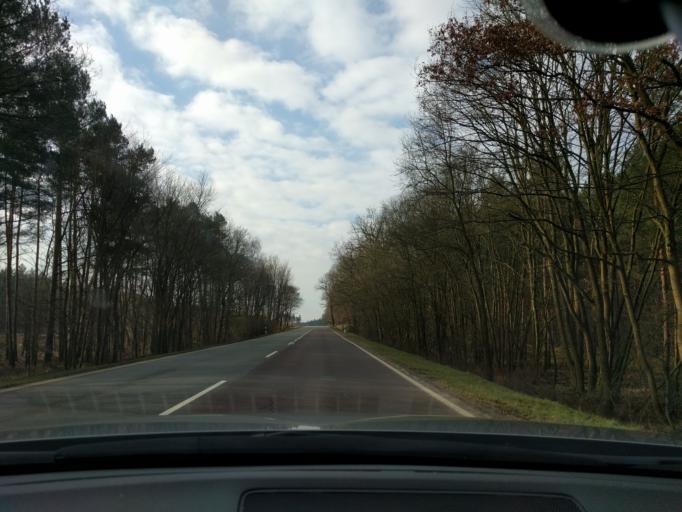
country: DE
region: Saxony-Anhalt
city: Colbitz
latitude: 52.3725
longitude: 11.6173
